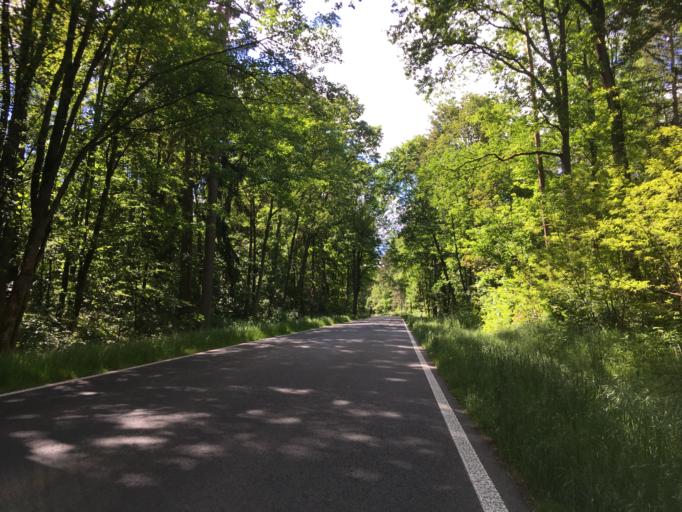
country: DE
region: Brandenburg
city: Protzel
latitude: 52.6013
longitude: 13.9928
